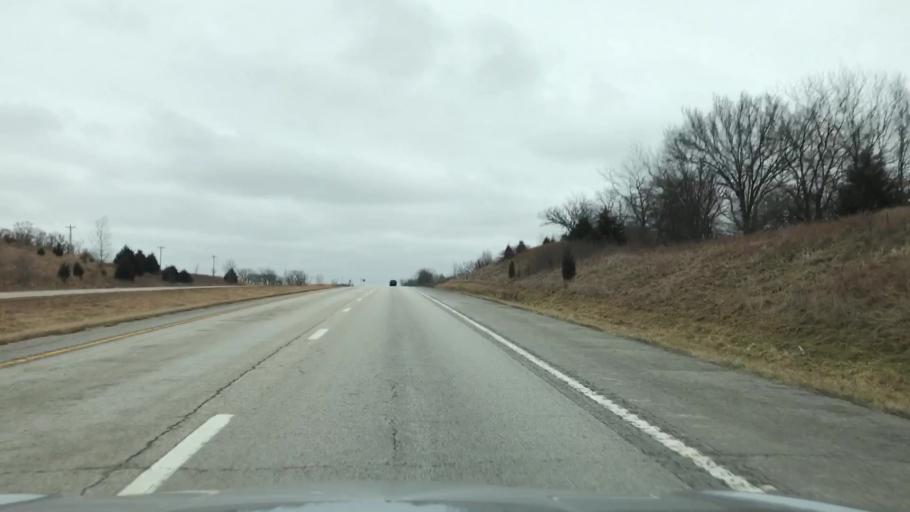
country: US
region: Missouri
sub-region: Clinton County
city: Cameron
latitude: 39.7511
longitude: -94.1524
